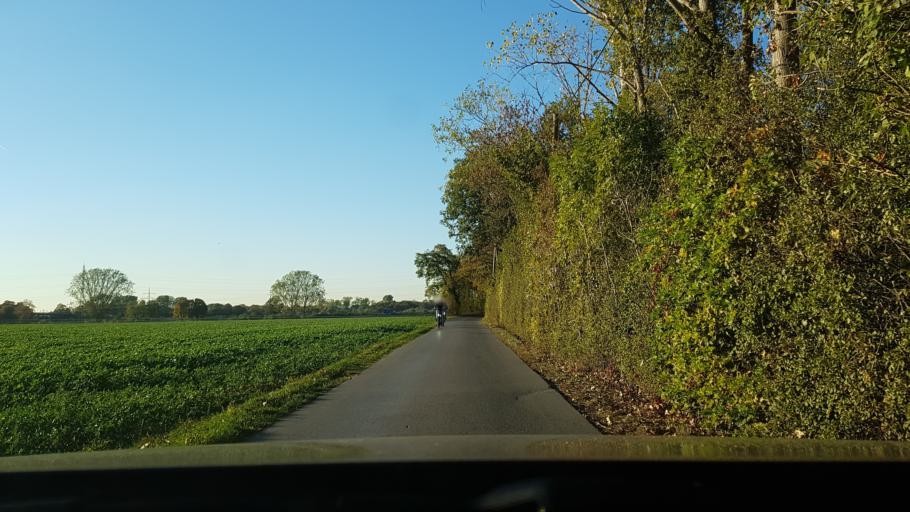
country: DE
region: North Rhine-Westphalia
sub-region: Regierungsbezirk Dusseldorf
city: Moers
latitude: 51.4292
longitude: 6.5844
